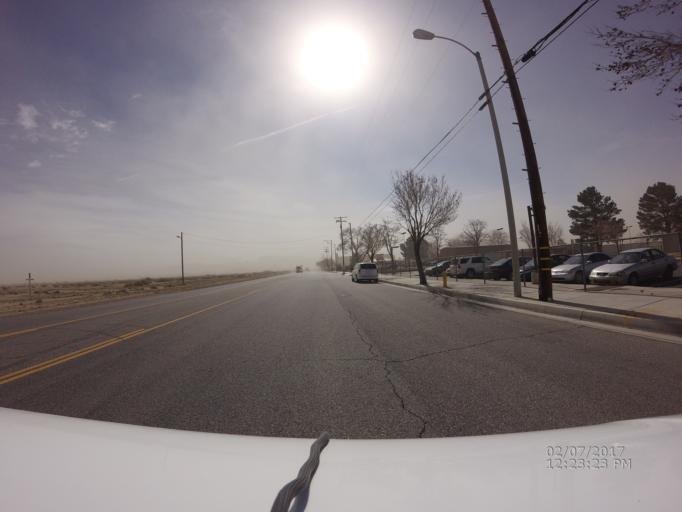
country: US
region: California
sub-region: Los Angeles County
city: Lake Los Angeles
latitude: 34.6406
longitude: -117.8273
